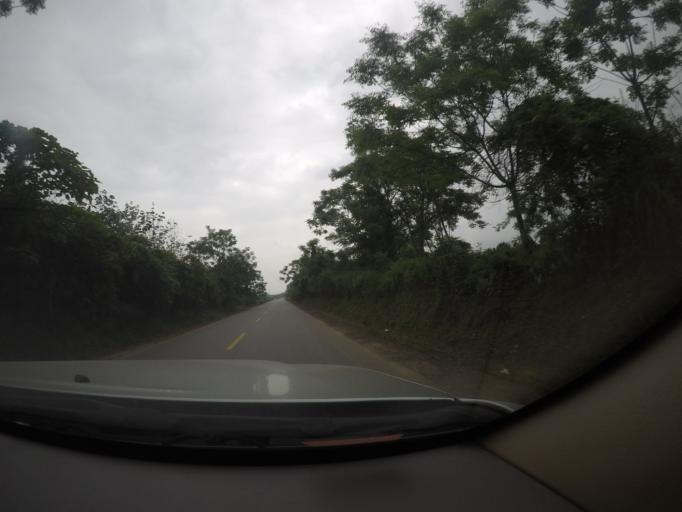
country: VN
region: Quang Binh
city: Hoan Lao
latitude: 17.5978
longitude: 106.4214
